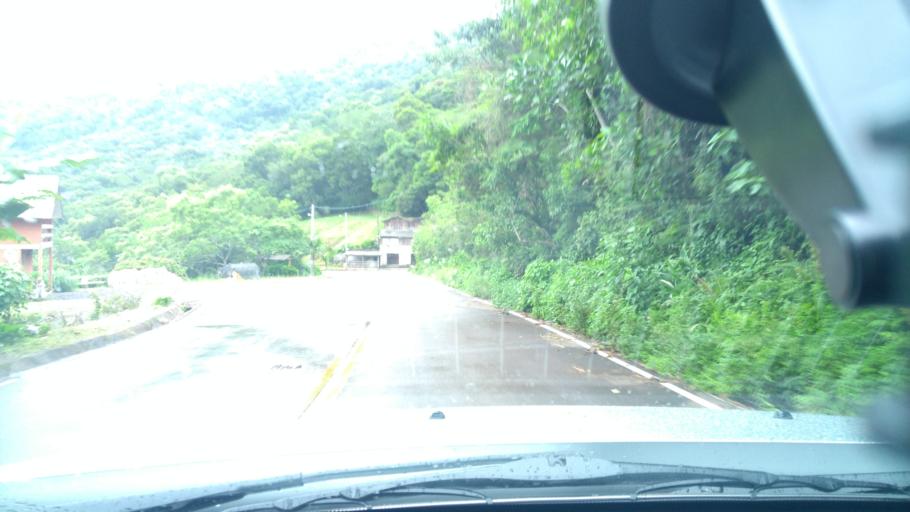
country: BR
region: Rio Grande do Sul
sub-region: Torres
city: Torres
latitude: -29.1855
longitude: -49.9879
